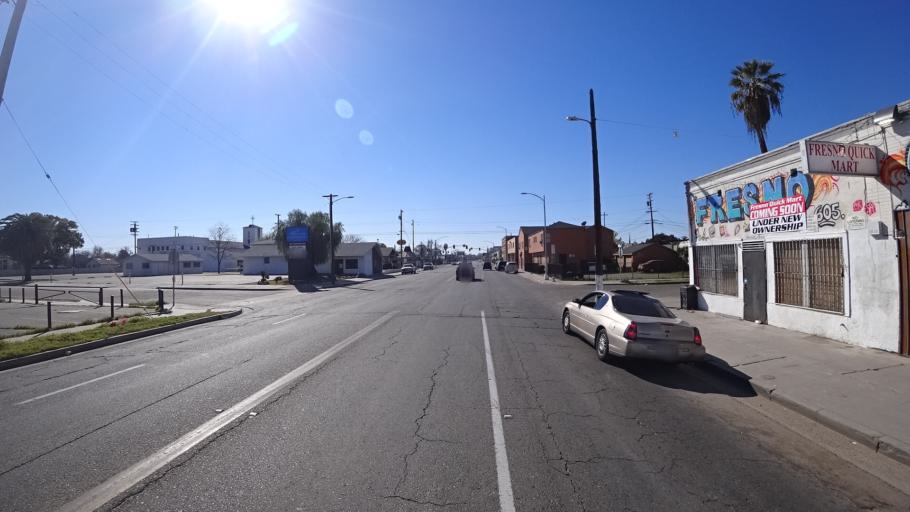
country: US
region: California
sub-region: Fresno County
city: Fresno
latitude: 36.7517
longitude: -119.7815
